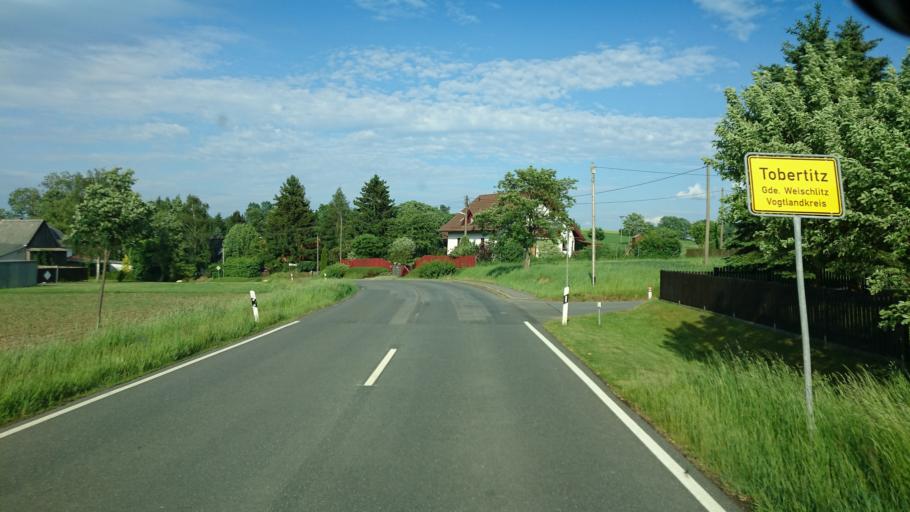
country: DE
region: Saxony
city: Reuth
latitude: 50.4806
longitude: 11.9909
